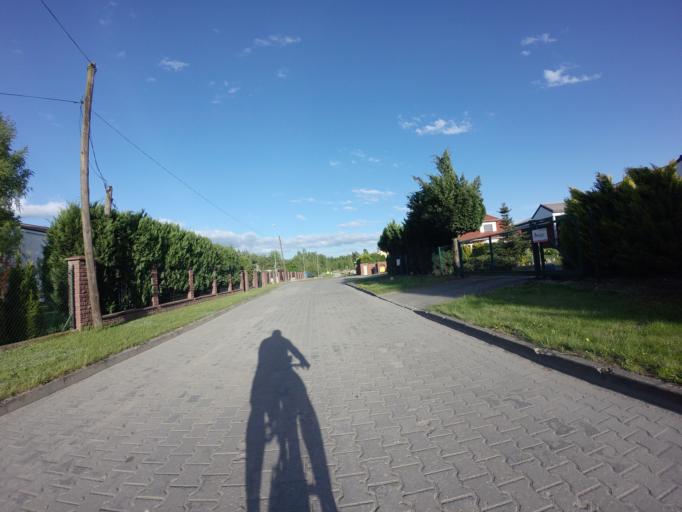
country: PL
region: West Pomeranian Voivodeship
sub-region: Powiat choszczenski
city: Choszczno
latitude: 53.1573
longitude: 15.4197
